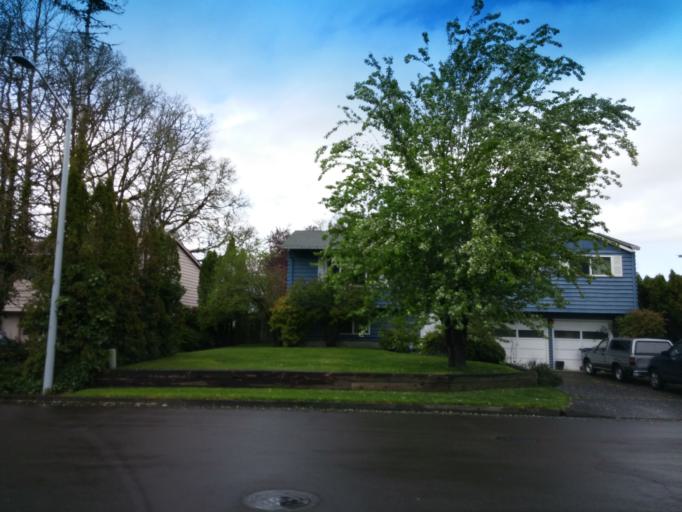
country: US
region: Oregon
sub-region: Washington County
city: Aloha
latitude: 45.5094
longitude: -122.8641
